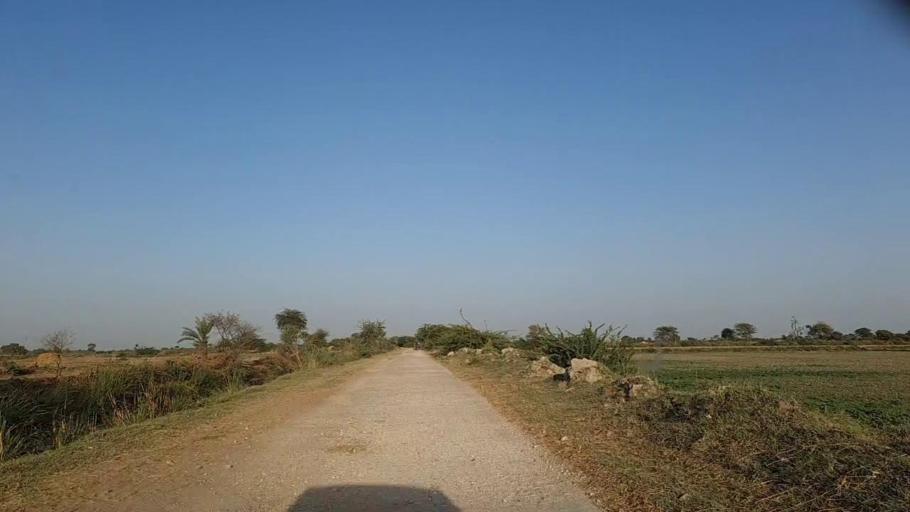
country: PK
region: Sindh
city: Jati
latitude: 24.4138
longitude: 68.3301
